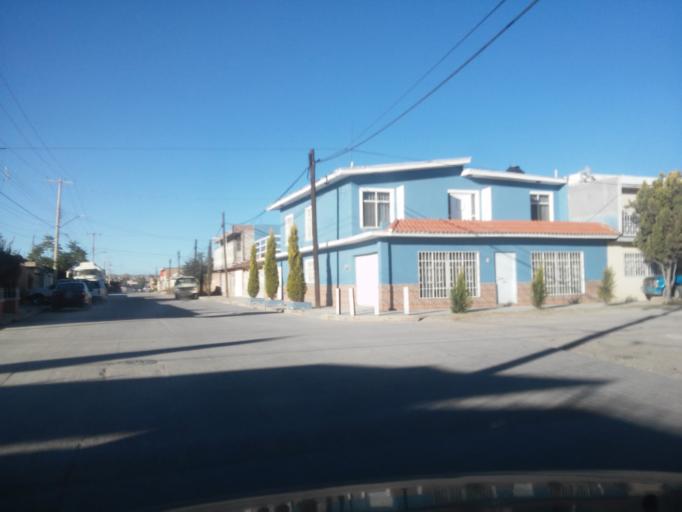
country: MX
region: Durango
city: Victoria de Durango
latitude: 24.0149
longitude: -104.6365
